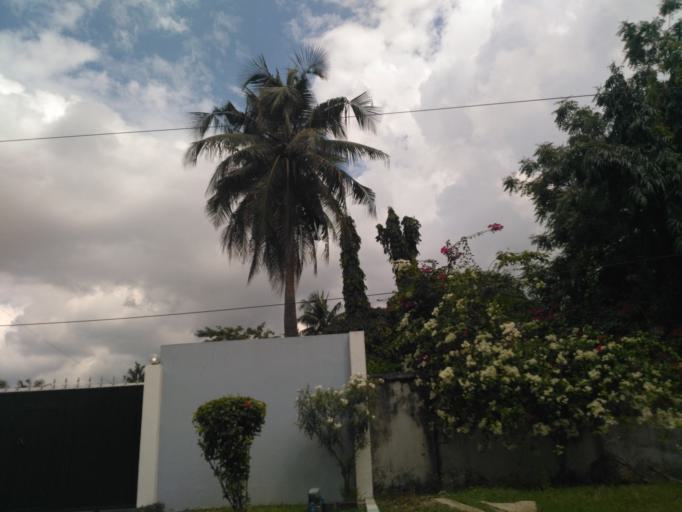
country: TZ
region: Dar es Salaam
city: Magomeni
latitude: -6.7587
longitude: 39.2457
